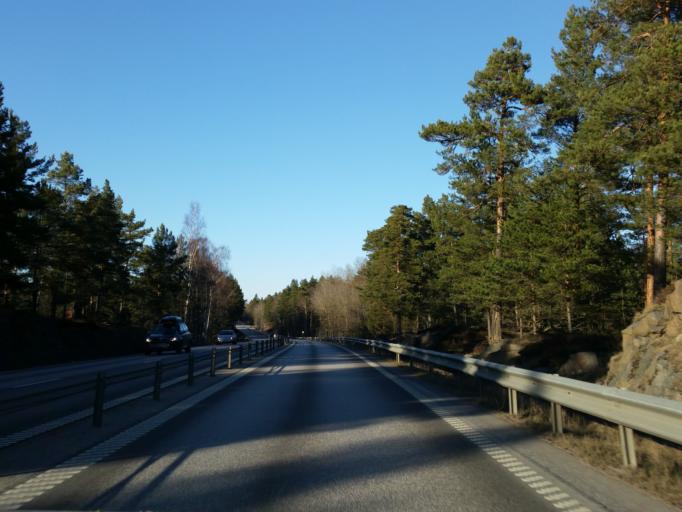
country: SE
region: Kalmar
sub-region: Oskarshamns Kommun
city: Oskarshamn
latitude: 57.3232
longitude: 16.4735
